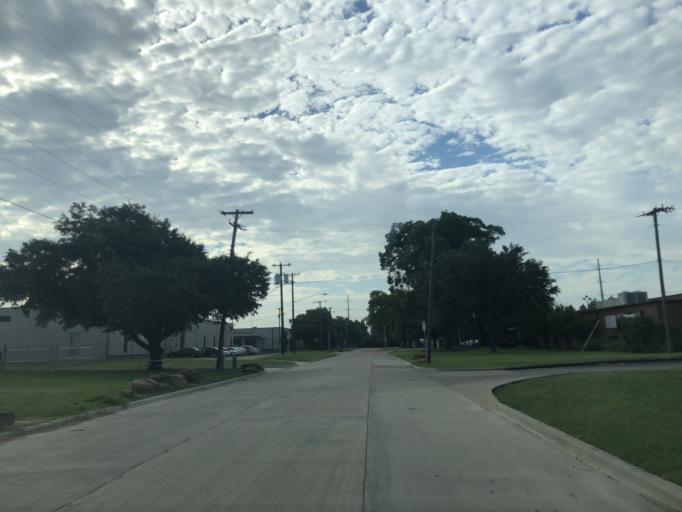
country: US
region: Texas
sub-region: Dallas County
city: Irving
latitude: 32.8162
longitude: -96.8964
